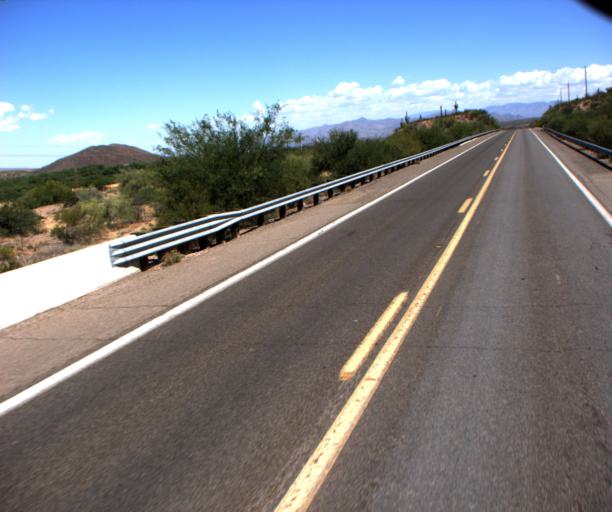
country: US
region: Arizona
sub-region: Pinal County
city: Mammoth
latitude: 32.8909
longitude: -110.7162
